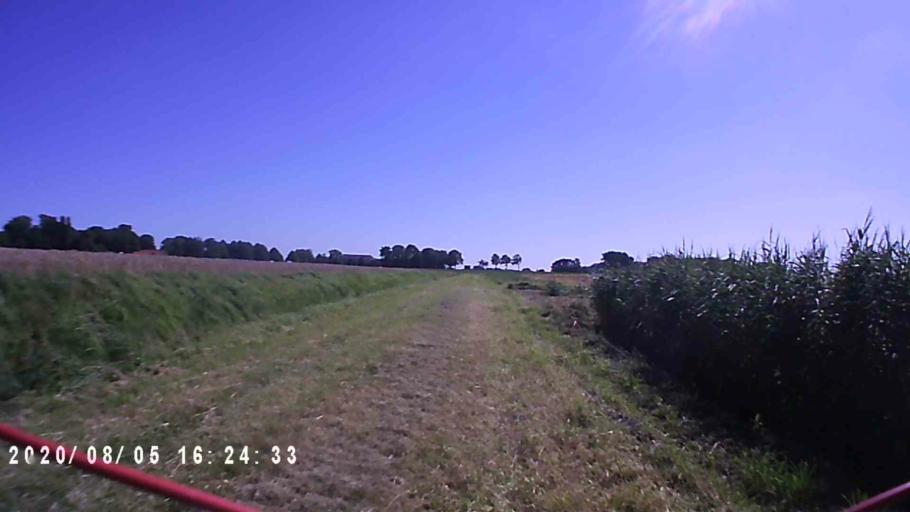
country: NL
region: Groningen
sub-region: Gemeente Winsum
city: Winsum
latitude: 53.3871
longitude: 6.5353
